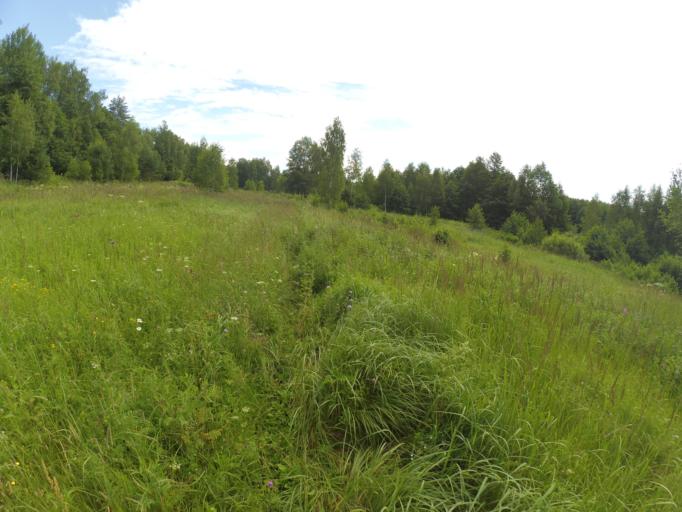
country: RU
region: Moskovskaya
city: Fosforitnyy
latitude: 55.3352
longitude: 38.9182
